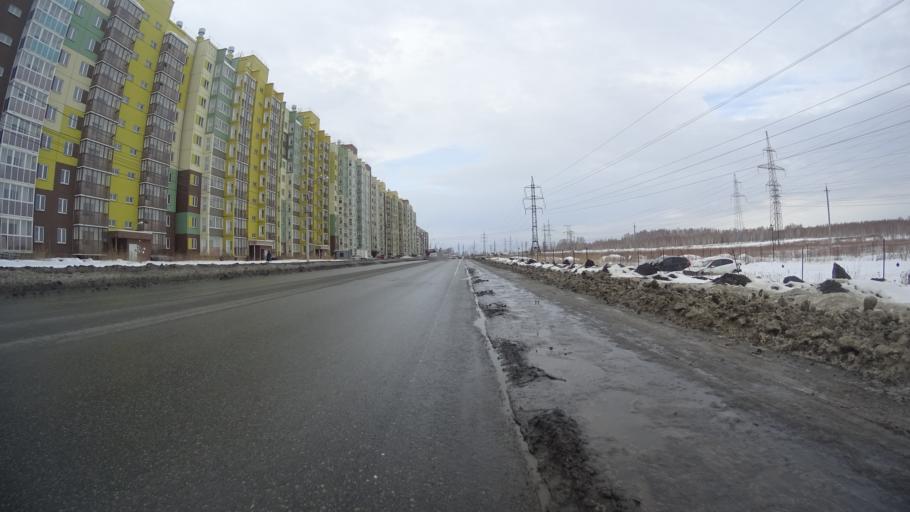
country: RU
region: Chelyabinsk
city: Roshchino
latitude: 55.2161
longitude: 61.3029
